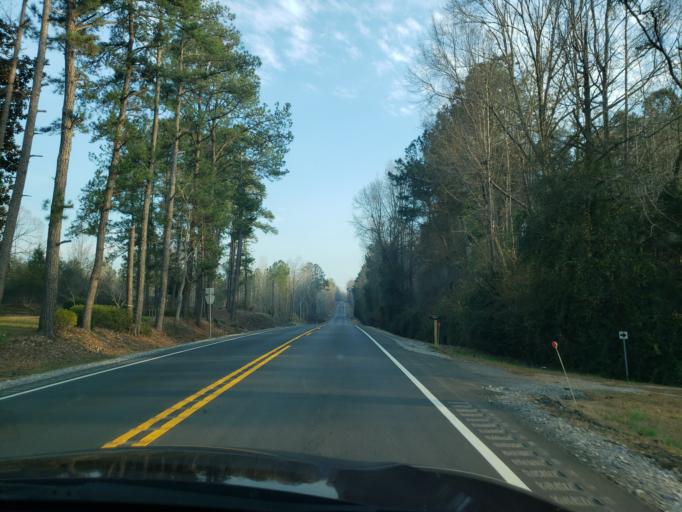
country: US
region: Alabama
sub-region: Hale County
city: Greensboro
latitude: 32.8182
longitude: -87.5990
